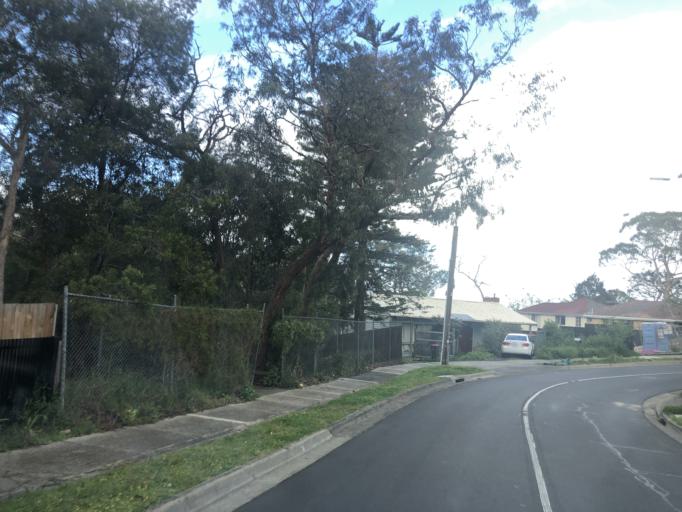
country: AU
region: Victoria
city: Burwood East
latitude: -37.8662
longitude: 145.1350
